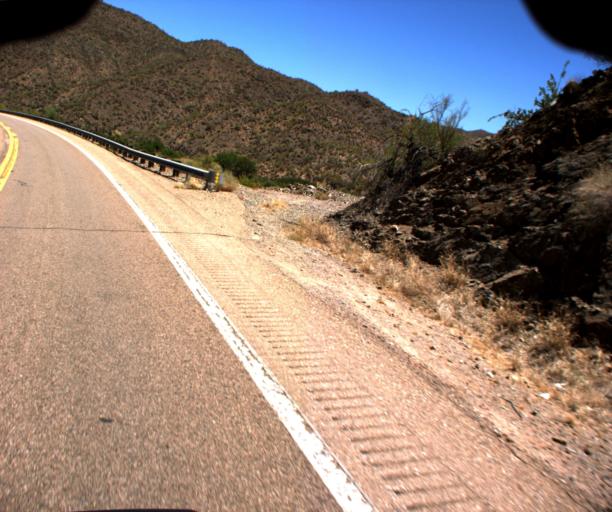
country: US
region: Arizona
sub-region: Pinal County
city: Kearny
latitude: 33.0463
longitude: -110.7179
